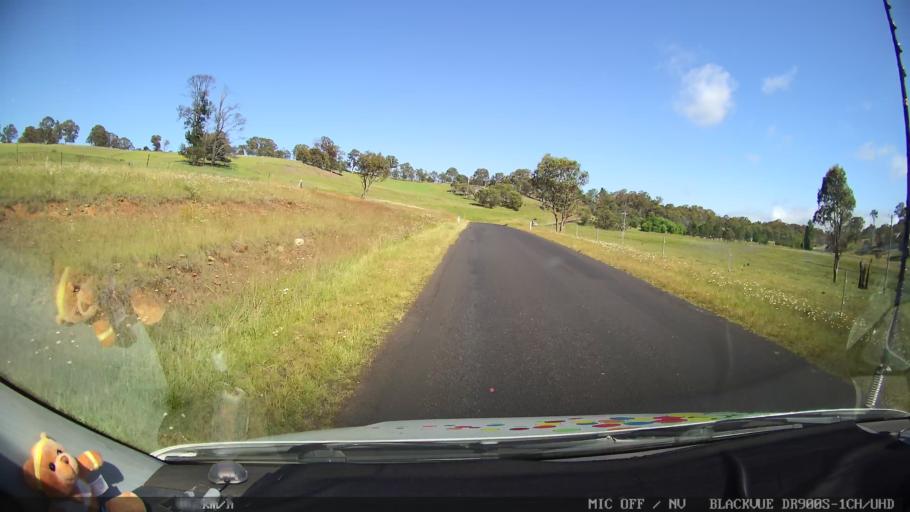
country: AU
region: New South Wales
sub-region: Guyra
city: Guyra
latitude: -30.1140
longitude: 151.6853
